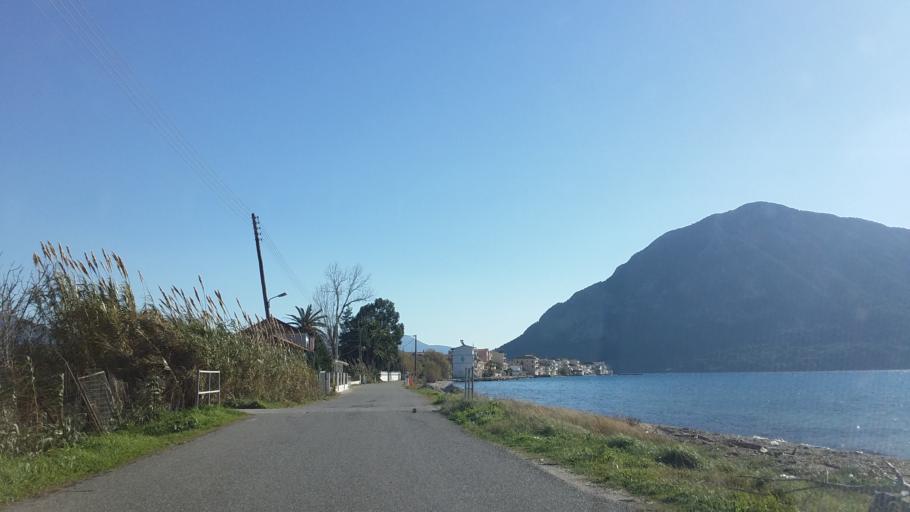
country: GR
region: West Greece
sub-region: Nomos Aitolias kai Akarnanias
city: Kandila
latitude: 38.6746
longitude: 20.9401
